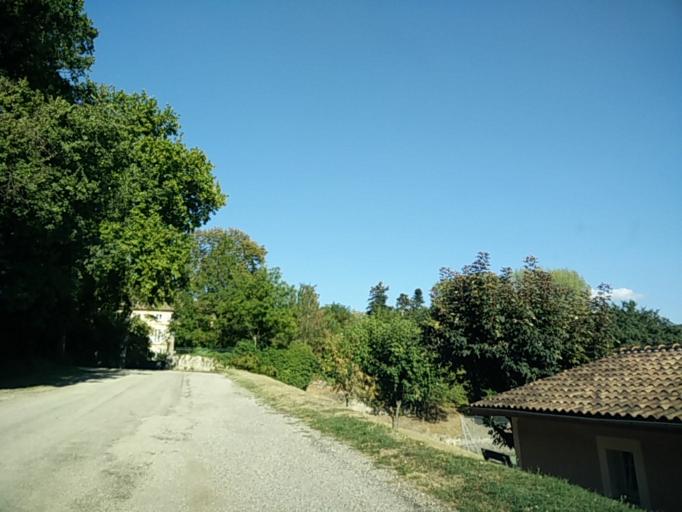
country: FR
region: Rhone-Alpes
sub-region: Departement de la Drome
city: La Begude-de-Mazenc
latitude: 44.5465
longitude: 4.9316
